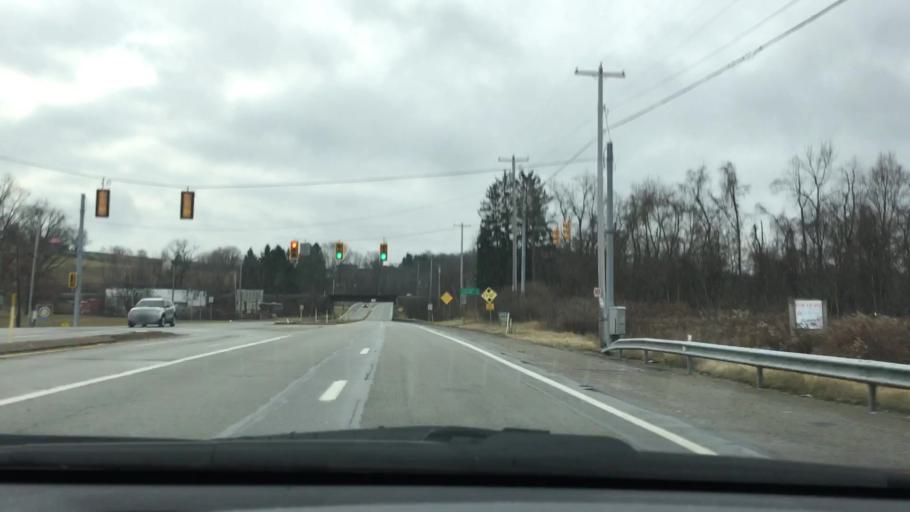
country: US
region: Pennsylvania
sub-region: Westmoreland County
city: West Newton
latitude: 40.1516
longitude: -79.7741
